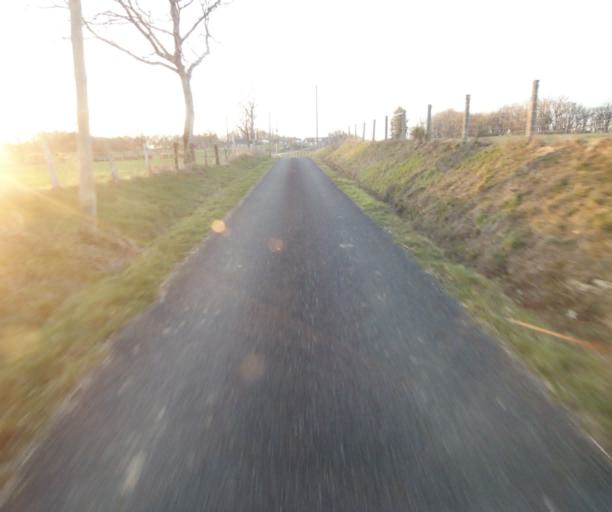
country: FR
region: Limousin
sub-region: Departement de la Correze
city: Uzerche
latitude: 45.3636
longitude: 1.6120
